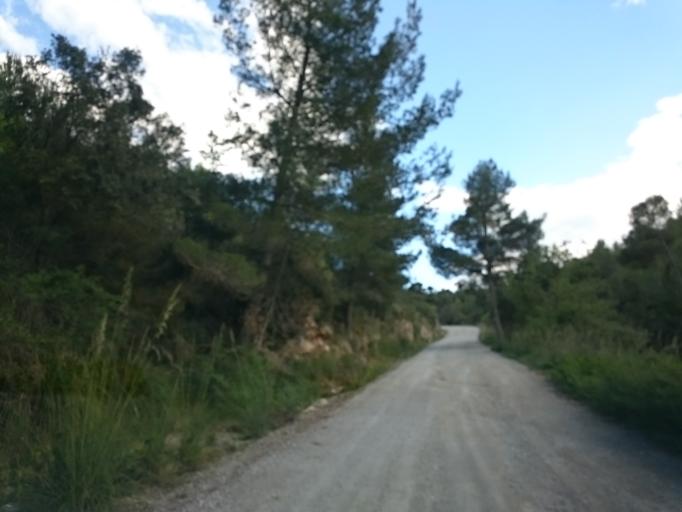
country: ES
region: Catalonia
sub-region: Provincia de Barcelona
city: Begues
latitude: 41.3196
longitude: 1.9224
